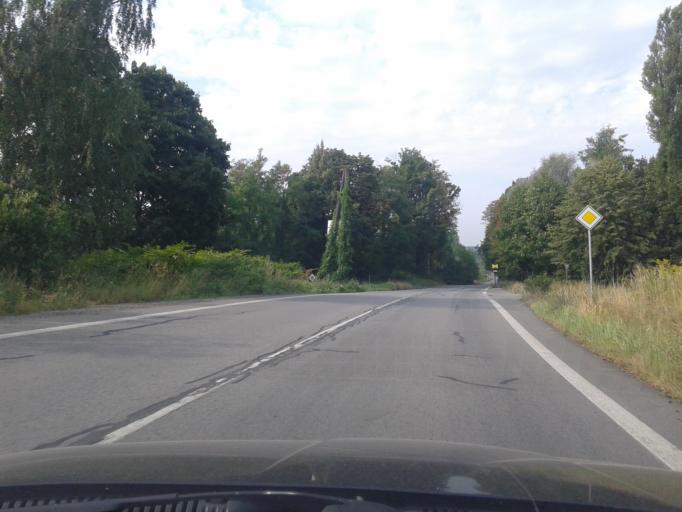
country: CZ
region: Moravskoslezsky
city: Orlova
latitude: 49.8434
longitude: 18.4496
